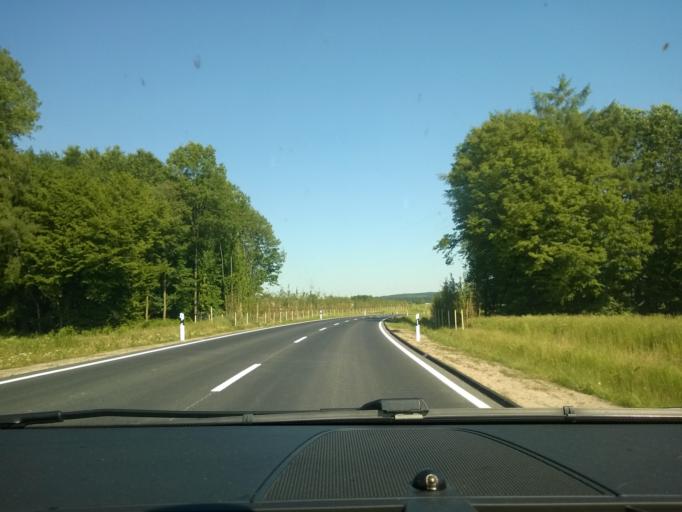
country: DE
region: North Rhine-Westphalia
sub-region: Regierungsbezirk Munster
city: Nottuln
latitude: 51.9295
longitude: 7.3721
